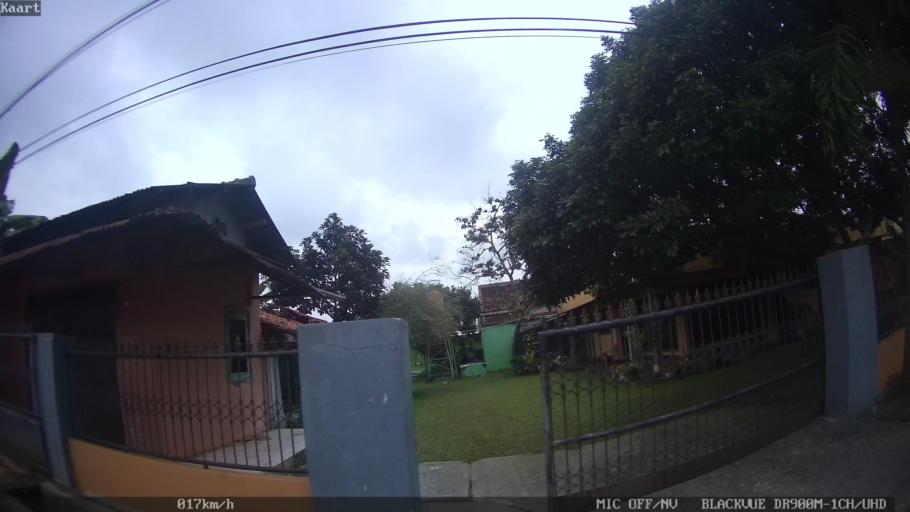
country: ID
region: Lampung
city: Bandarlampung
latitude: -5.4110
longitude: 105.2748
